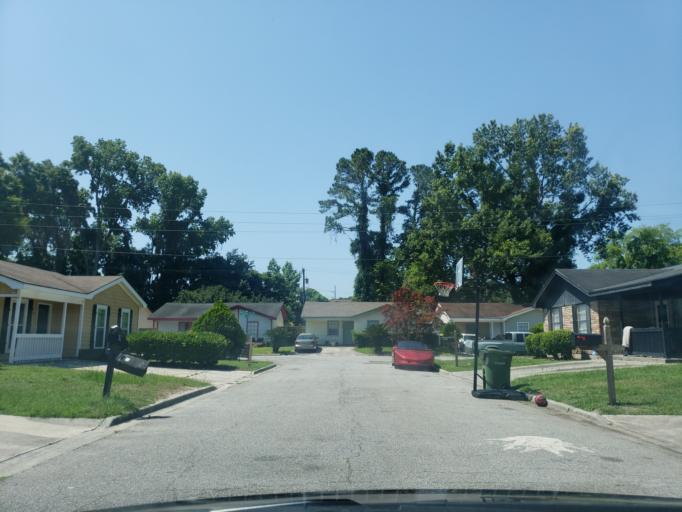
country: US
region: Georgia
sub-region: Chatham County
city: Montgomery
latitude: 31.9970
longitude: -81.1317
